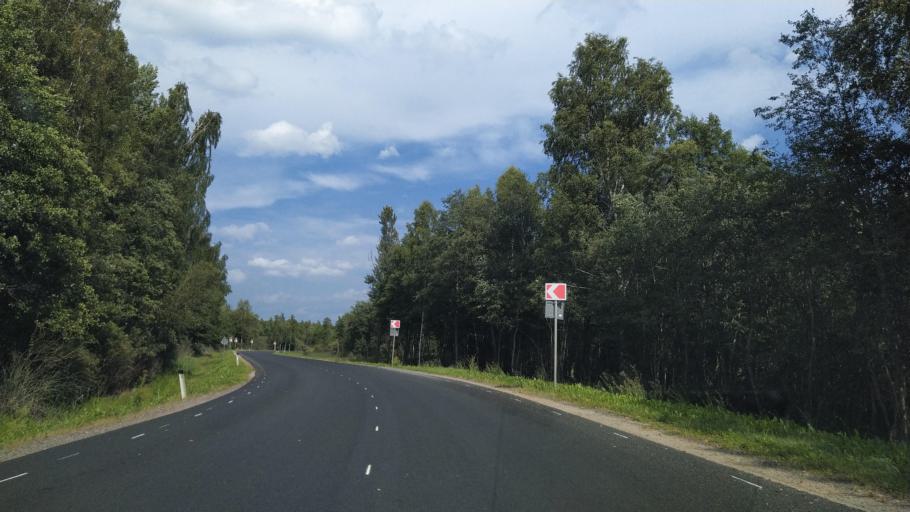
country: RU
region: Pskov
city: Vybor
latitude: 57.7388
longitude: 29.0126
